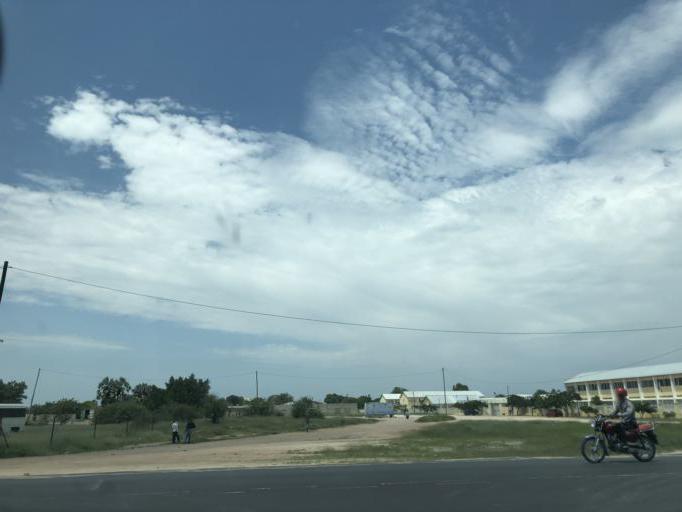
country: AO
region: Cunene
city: Ondjiva
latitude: -17.0935
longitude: 15.7467
